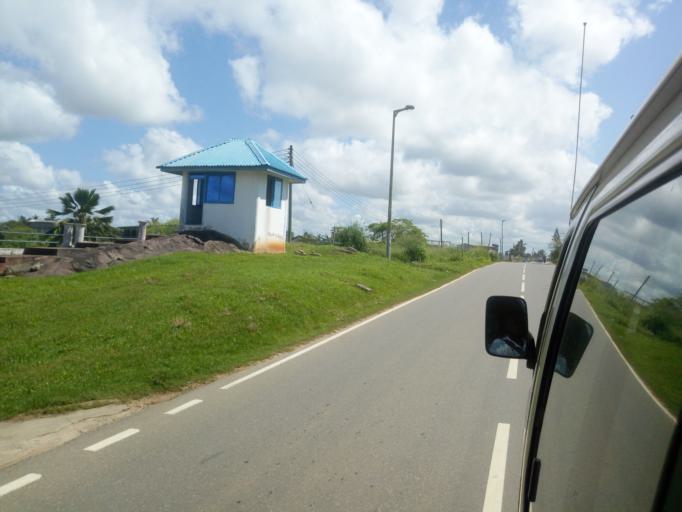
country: GH
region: Central
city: Elmina
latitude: 5.0938
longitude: -1.3382
